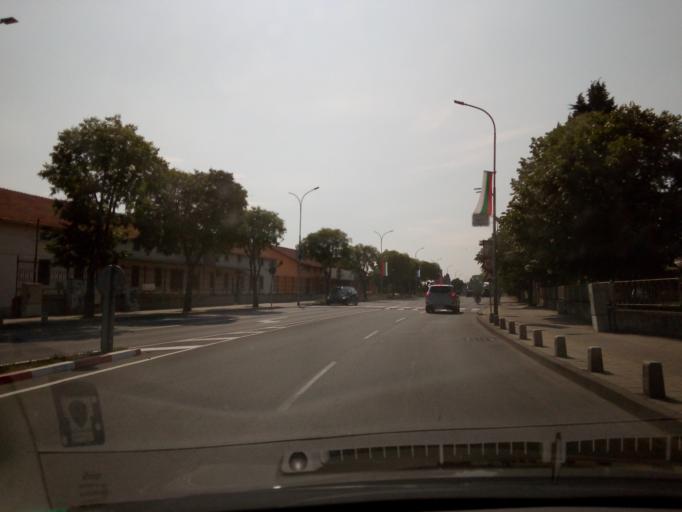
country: BG
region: Burgas
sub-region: Obshtina Pomorie
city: Pomorie
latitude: 42.5672
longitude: 27.6191
